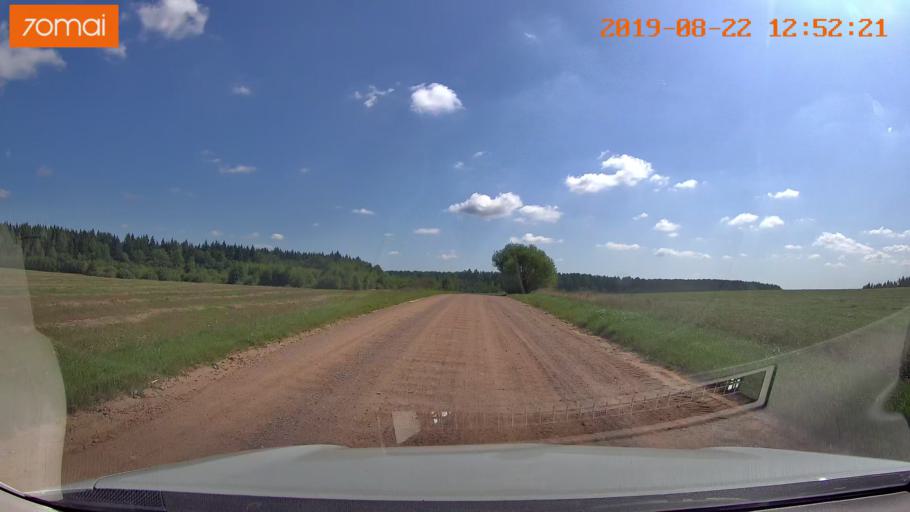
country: BY
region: Minsk
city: Prawdzinski
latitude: 53.4526
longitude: 27.6703
